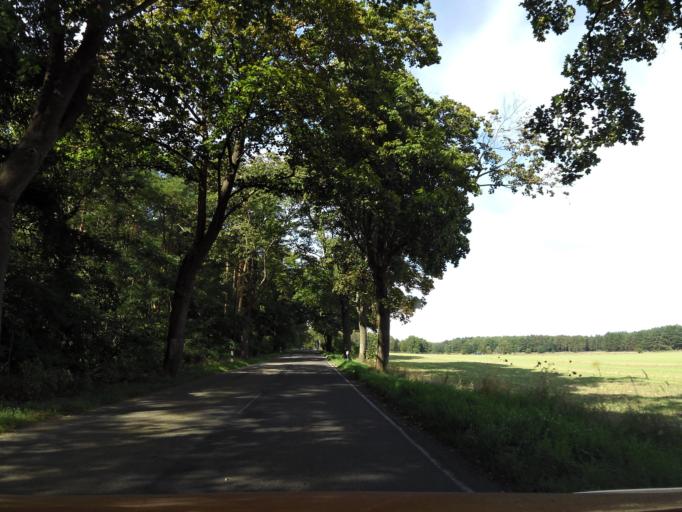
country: DE
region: Brandenburg
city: Michendorf
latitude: 52.2774
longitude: 13.1155
